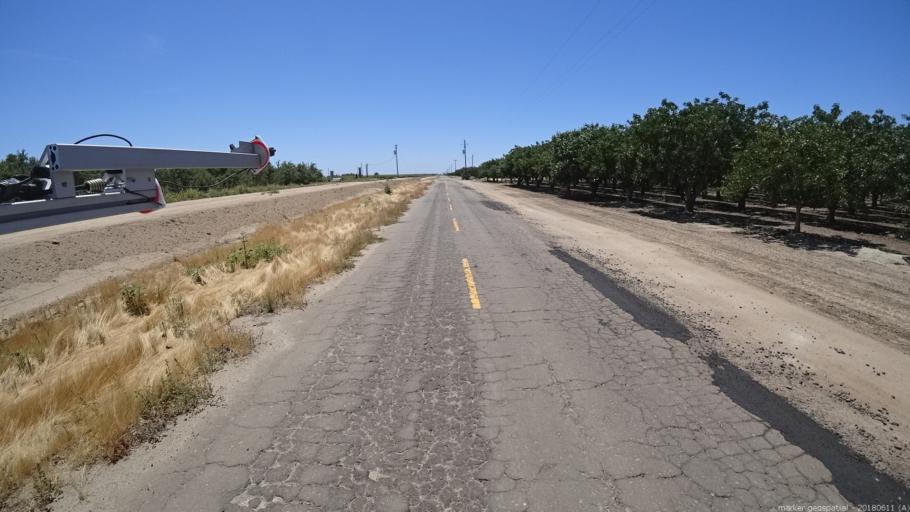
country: US
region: California
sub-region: Madera County
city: Fairmead
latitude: 37.0485
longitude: -120.2205
